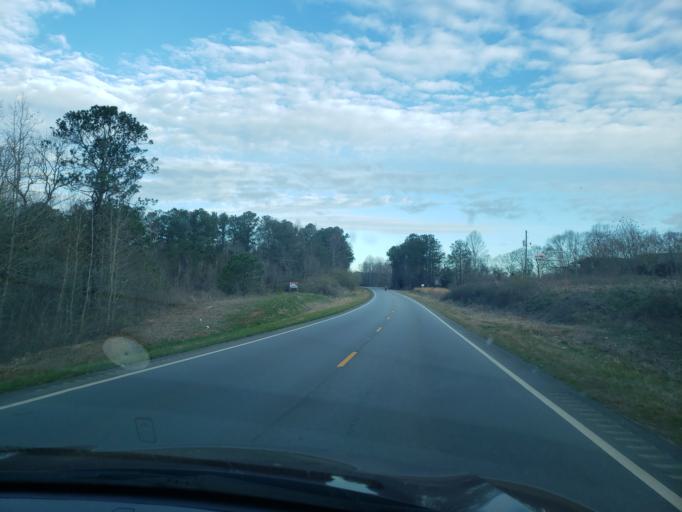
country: US
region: Alabama
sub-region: Randolph County
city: Wedowee
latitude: 33.2621
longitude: -85.4557
